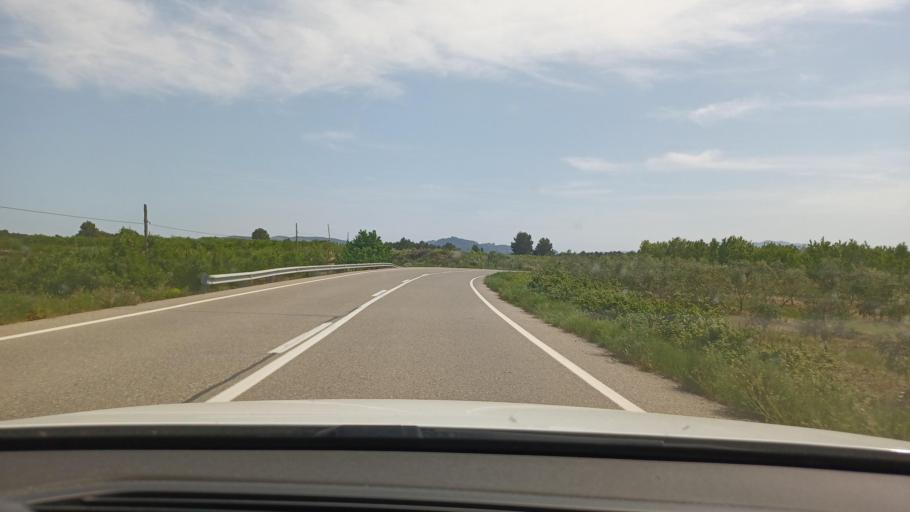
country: ES
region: Catalonia
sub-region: Provincia de Tarragona
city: Vilalba dels Arcs
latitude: 41.0918
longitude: 0.4193
